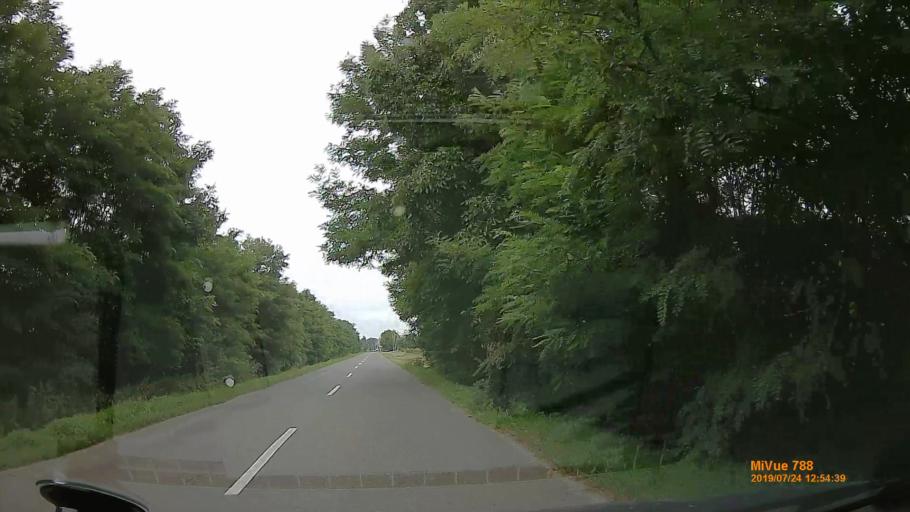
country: HU
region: Szabolcs-Szatmar-Bereg
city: Aranyosapati
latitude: 48.2179
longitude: 22.2971
